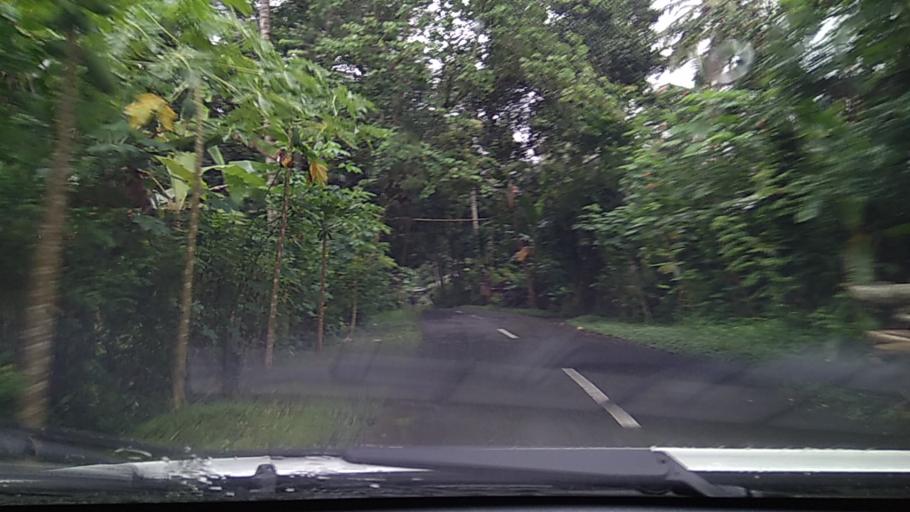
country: ID
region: Bali
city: Tiyingtali Kelod
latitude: -8.4123
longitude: 115.6231
